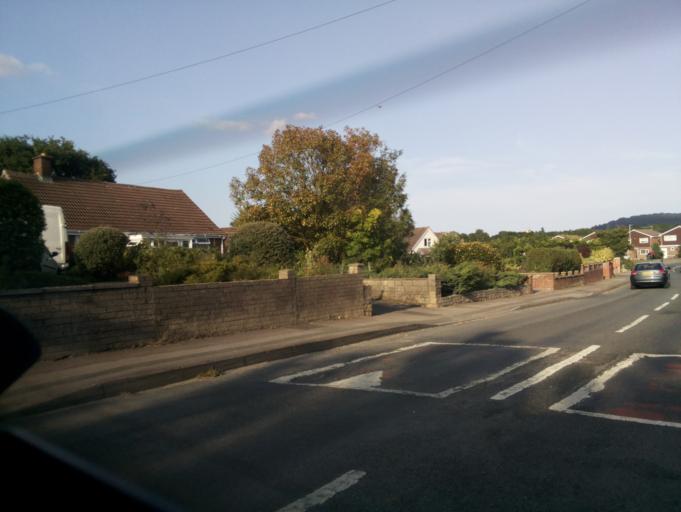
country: GB
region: England
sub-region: Gloucestershire
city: Barnwood
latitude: 51.8323
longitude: -2.2132
